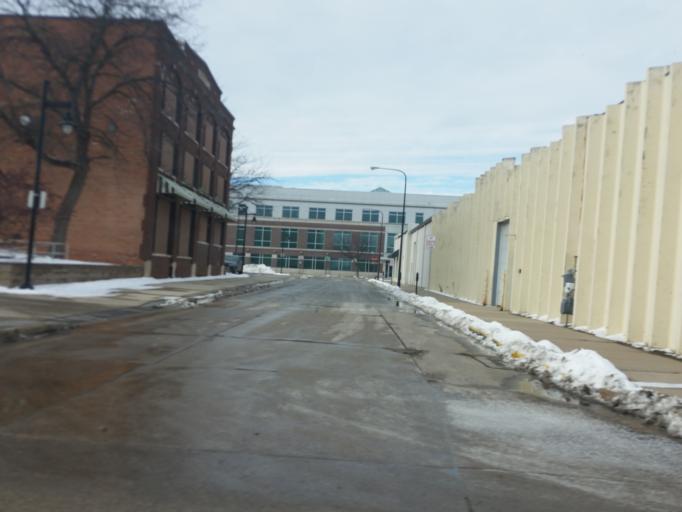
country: US
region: Iowa
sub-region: Black Hawk County
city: Waterloo
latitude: 42.4961
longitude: -92.3348
